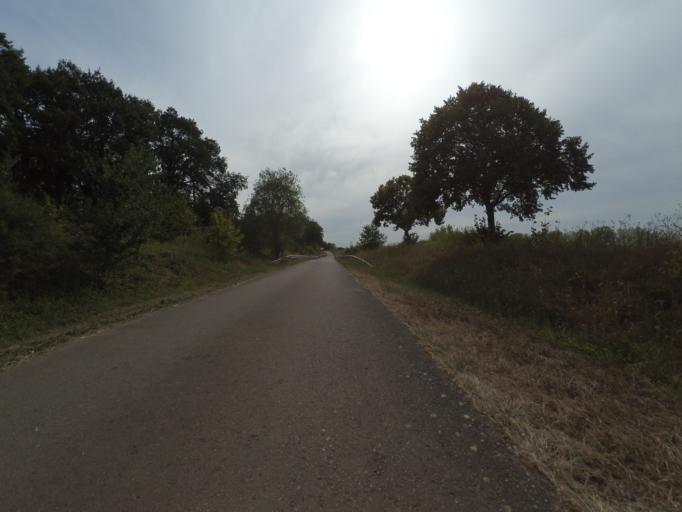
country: LU
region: Grevenmacher
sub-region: Canton de Remich
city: Mondorf-les-Bains
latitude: 49.5099
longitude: 6.3012
